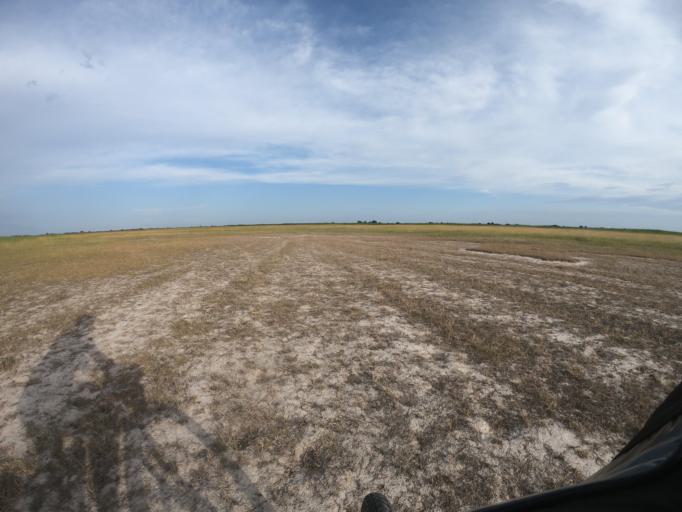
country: HU
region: Hajdu-Bihar
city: Hortobagy
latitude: 47.6023
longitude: 21.0602
